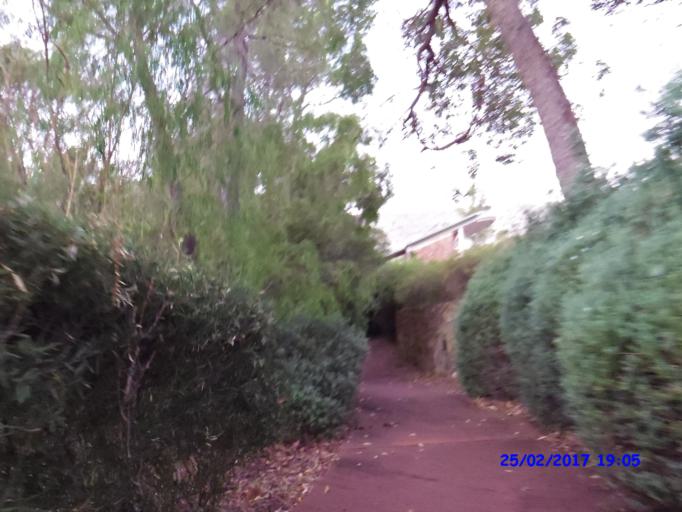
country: AU
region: Western Australia
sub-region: Harvey
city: Harvey
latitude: -33.0791
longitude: 115.9285
